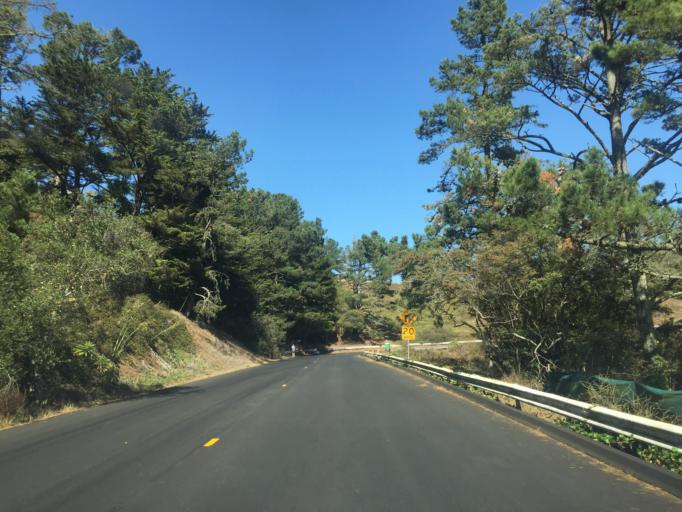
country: US
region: California
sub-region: San Francisco County
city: San Francisco
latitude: 37.7487
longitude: -122.4482
